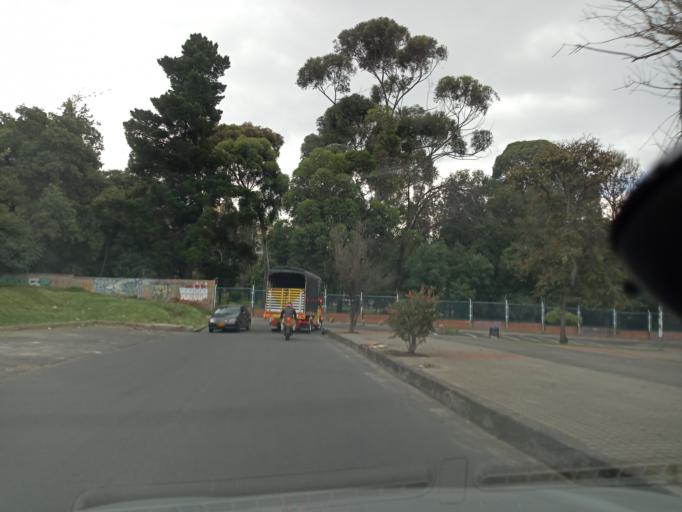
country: CO
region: Bogota D.C.
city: Bogota
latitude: 4.5700
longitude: -74.1061
